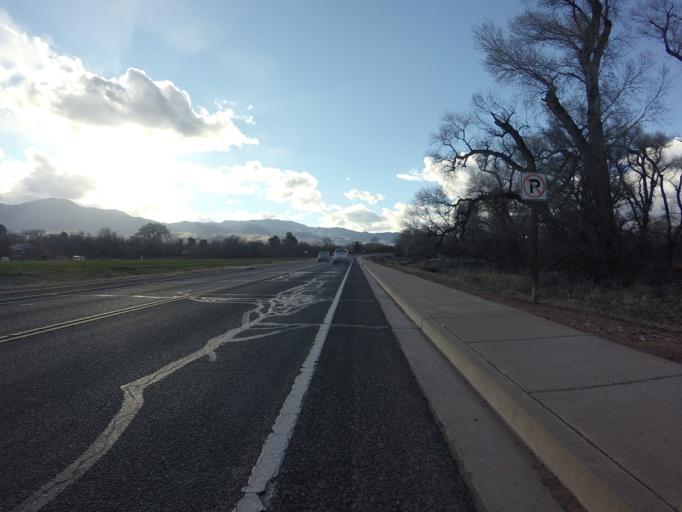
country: US
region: Arizona
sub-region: Yavapai County
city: Cottonwood
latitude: 34.7482
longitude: -112.0193
